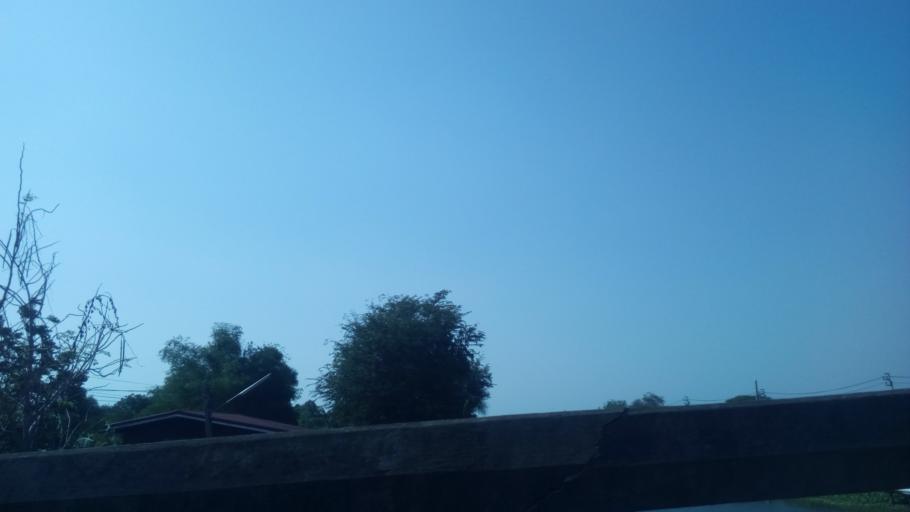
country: TH
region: Nonthaburi
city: Bang Yai
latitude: 13.8758
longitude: 100.2936
